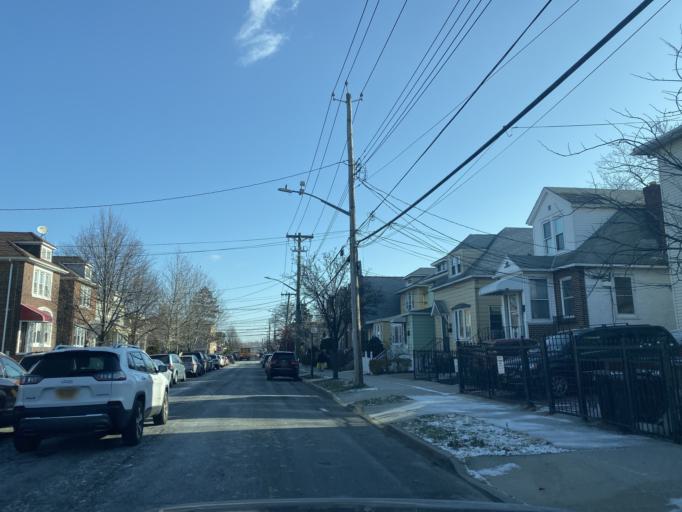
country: US
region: New York
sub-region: Bronx
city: The Bronx
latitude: 40.8264
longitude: -73.8481
